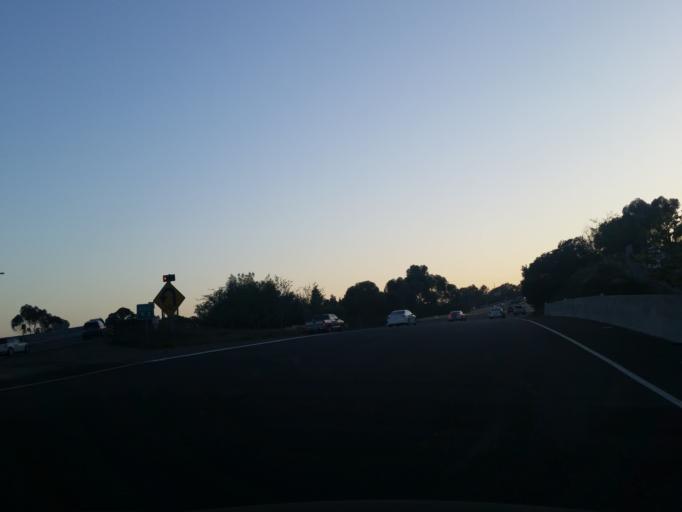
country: US
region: California
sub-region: San Diego County
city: San Diego
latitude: 32.7173
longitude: -117.1189
